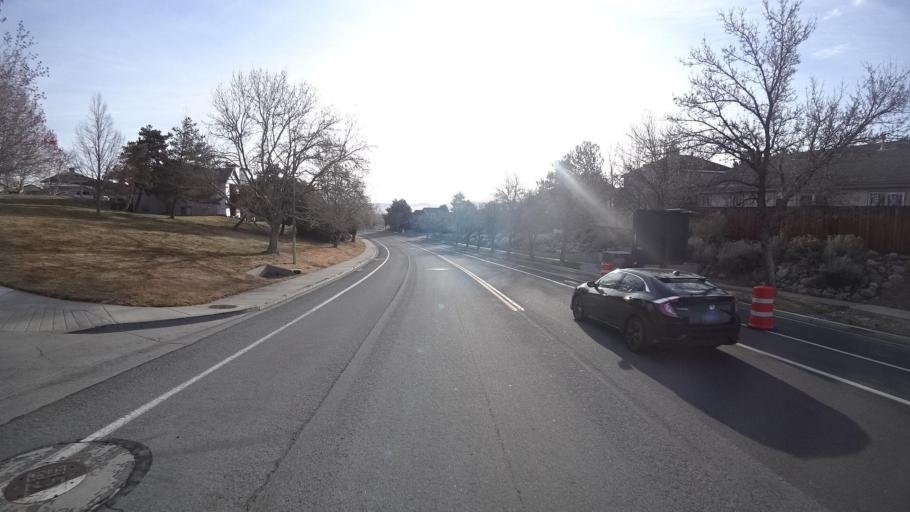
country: US
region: Nevada
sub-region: Washoe County
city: Reno
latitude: 39.5184
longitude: -119.8525
